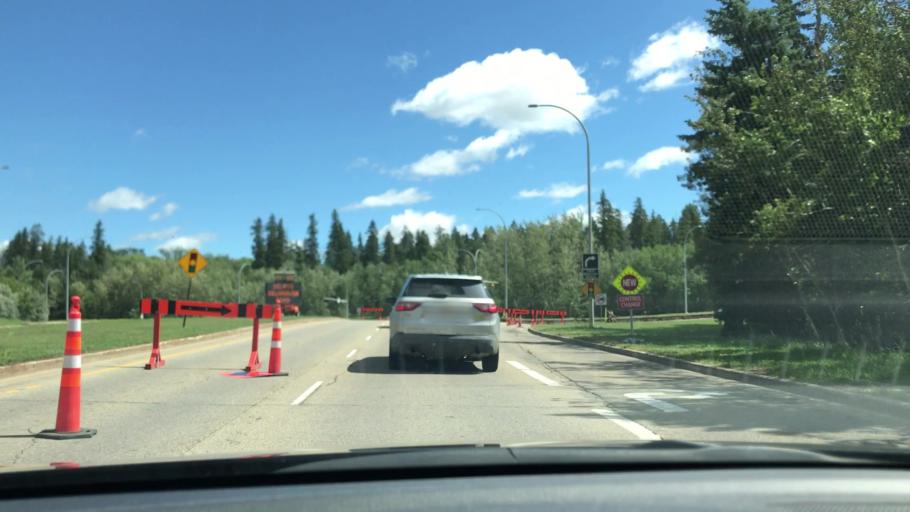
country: CA
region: Alberta
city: Edmonton
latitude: 53.5046
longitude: -113.5408
